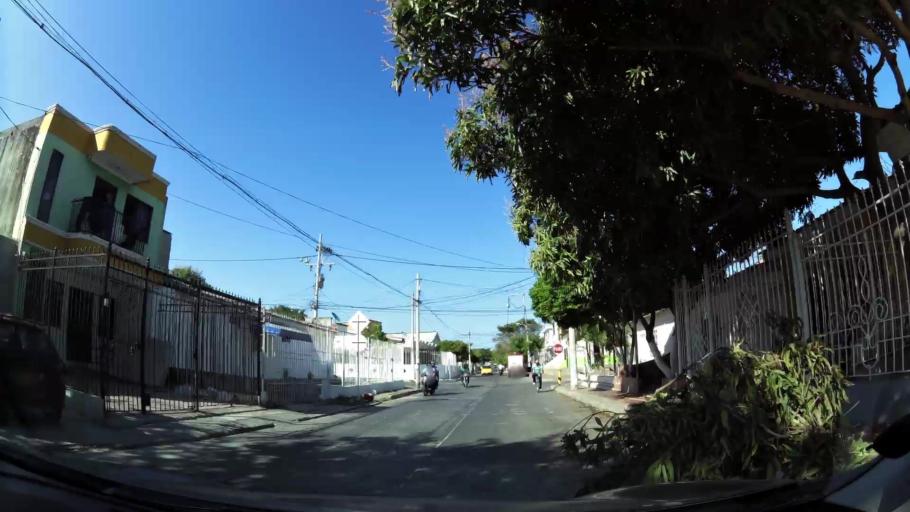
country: CO
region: Atlantico
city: Barranquilla
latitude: 10.9661
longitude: -74.7854
